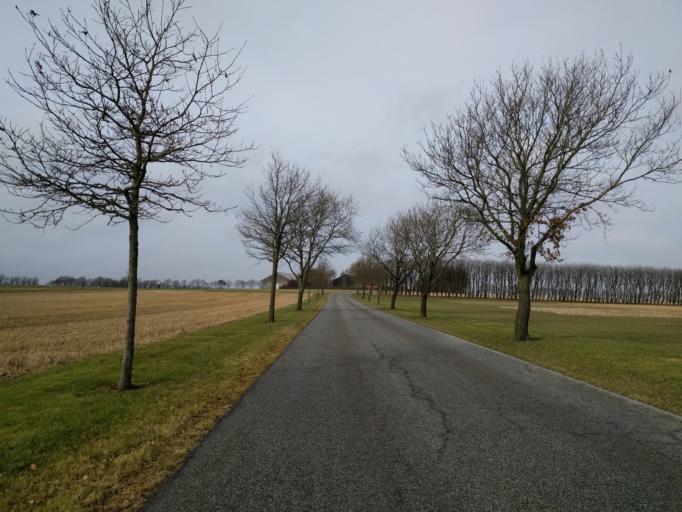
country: DK
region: Central Jutland
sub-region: Viborg Kommune
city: Bjerringbro
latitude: 56.4921
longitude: 9.5732
